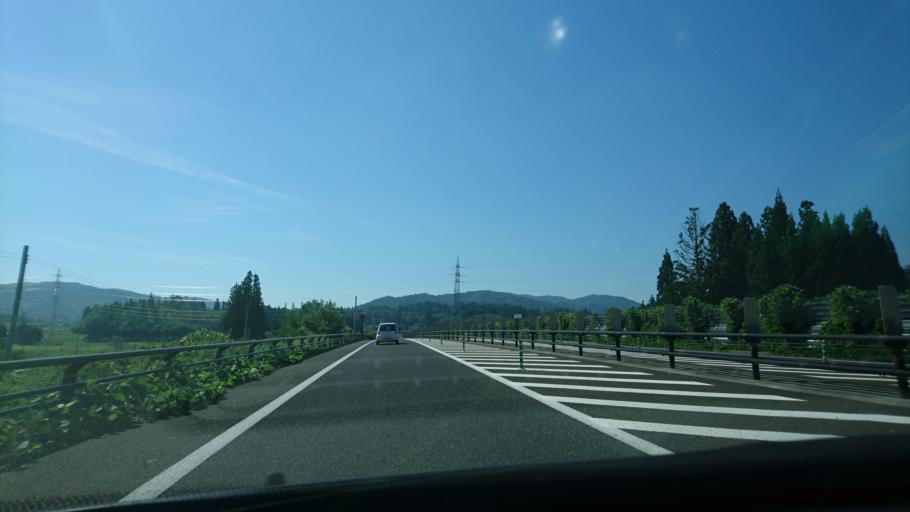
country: JP
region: Iwate
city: Hanamaki
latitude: 39.3514
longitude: 141.2403
